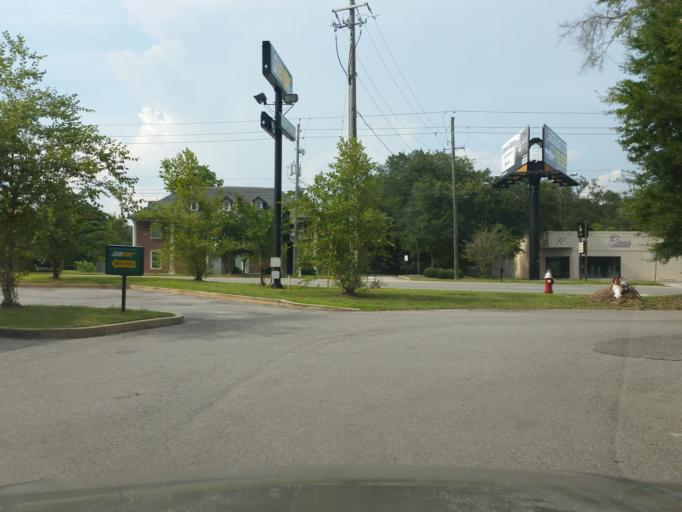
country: US
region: Florida
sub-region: Escambia County
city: Ferry Pass
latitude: 30.4955
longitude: -87.2123
